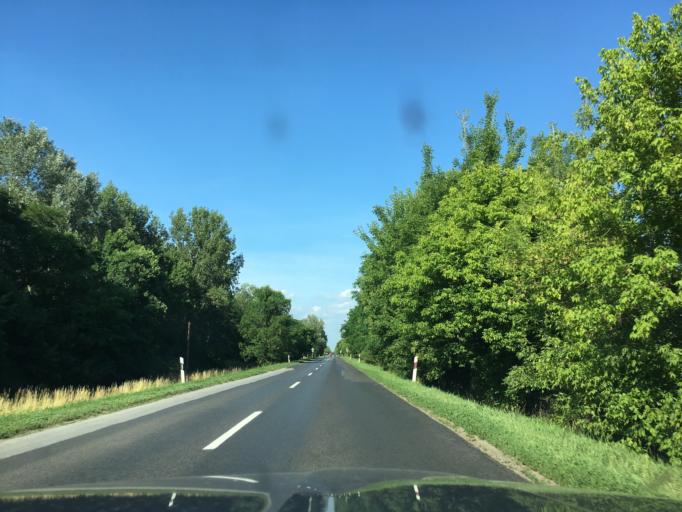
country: HU
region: Hajdu-Bihar
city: Debrecen
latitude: 47.5683
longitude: 21.6881
